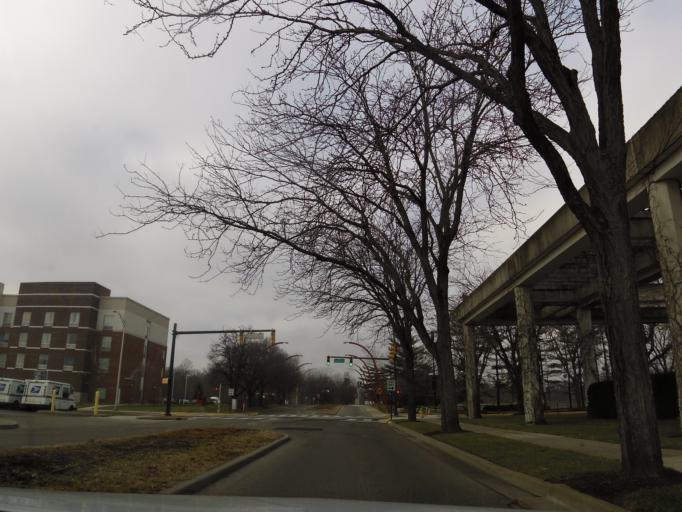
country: US
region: Indiana
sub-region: Bartholomew County
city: Columbus
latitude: 39.2034
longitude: -85.9232
